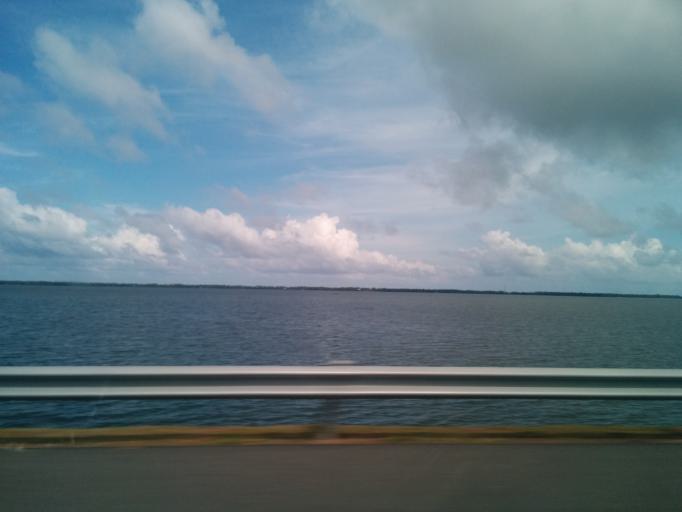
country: LK
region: Western
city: Katunayaka
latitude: 7.1402
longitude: 79.8677
